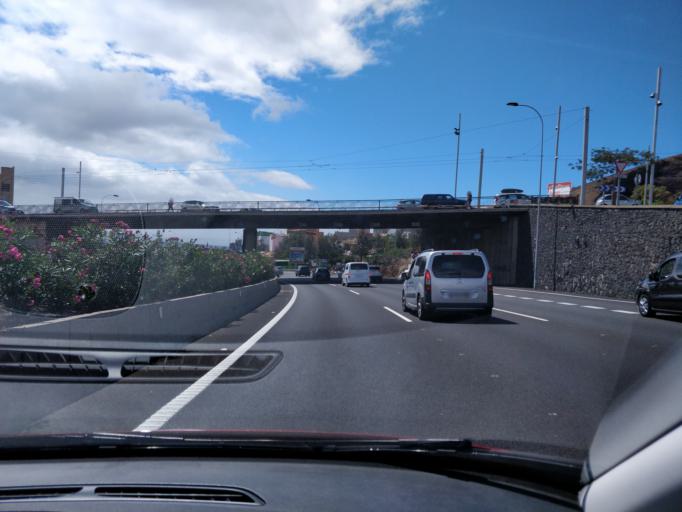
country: ES
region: Canary Islands
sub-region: Provincia de Santa Cruz de Tenerife
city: Santa Cruz de Tenerife
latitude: 28.4475
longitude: -16.2909
